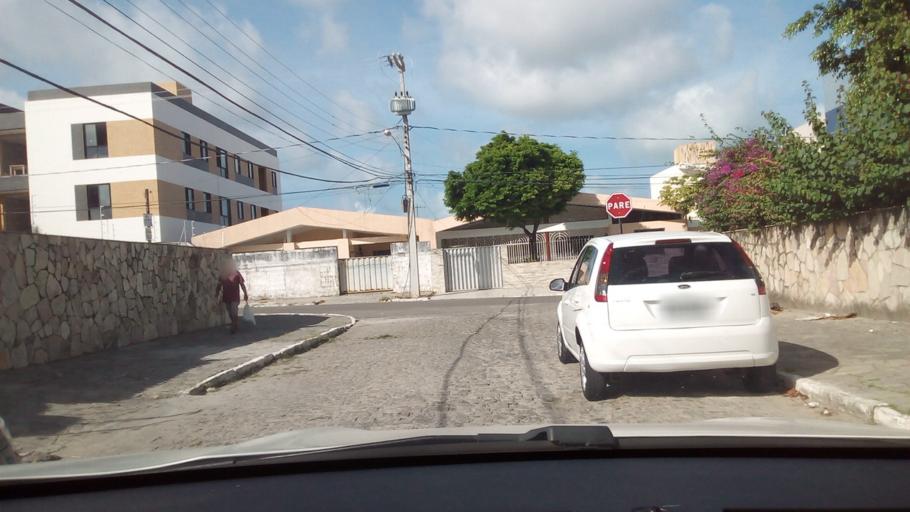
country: BR
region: Paraiba
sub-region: Joao Pessoa
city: Joao Pessoa
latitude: -7.1479
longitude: -34.8402
